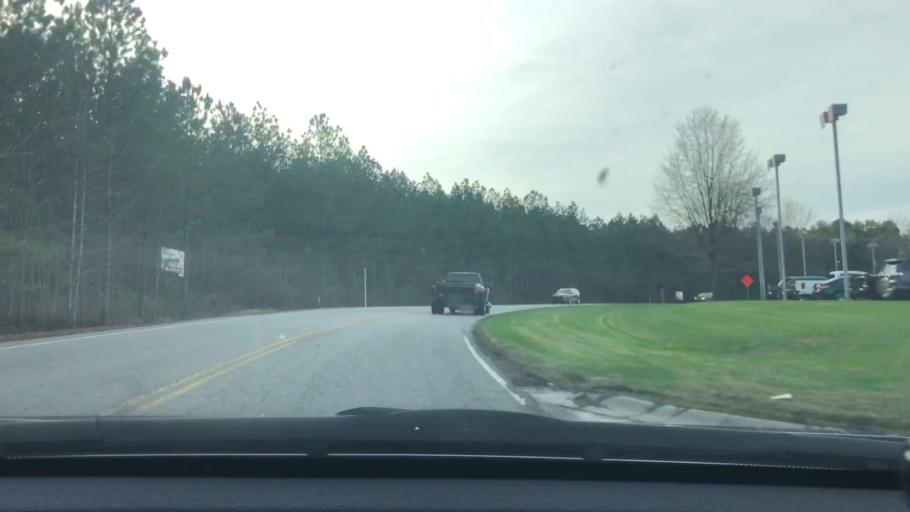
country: US
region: South Carolina
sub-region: Lexington County
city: Irmo
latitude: 34.0970
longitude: -81.1766
